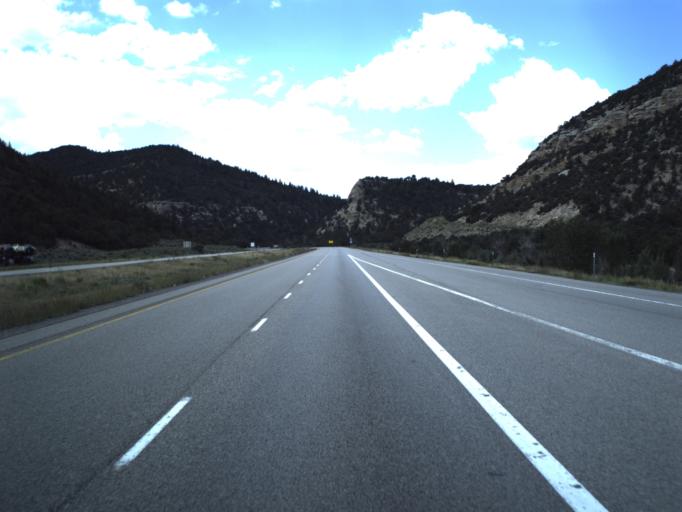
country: US
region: Utah
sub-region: Wayne County
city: Loa
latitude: 38.7572
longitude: -111.4299
